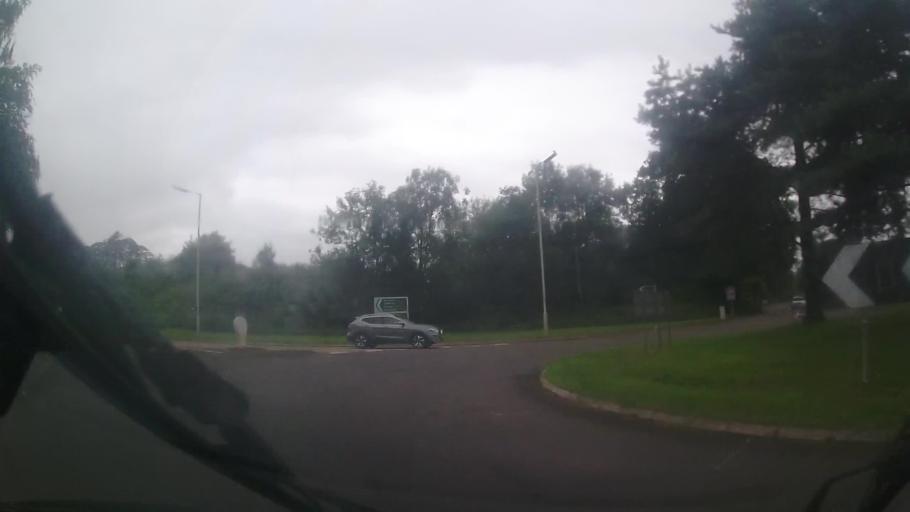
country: GB
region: England
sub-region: Shropshire
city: Whitchurch
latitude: 52.9579
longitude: -2.6745
